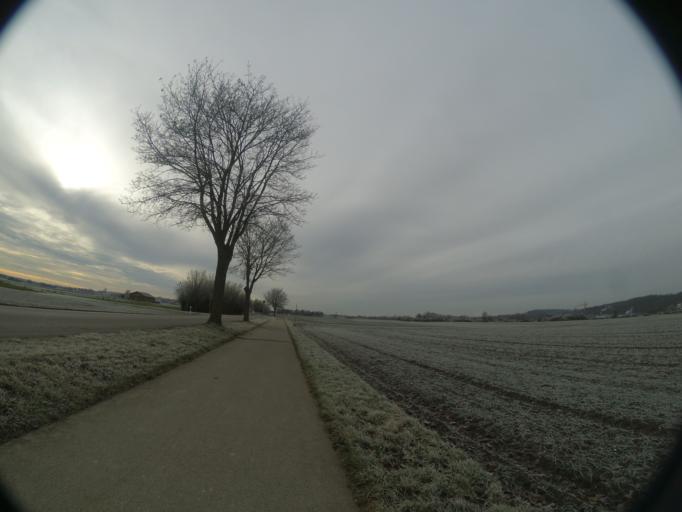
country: DE
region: Bavaria
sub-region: Swabia
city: Neu-Ulm
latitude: 48.4235
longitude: 10.0436
